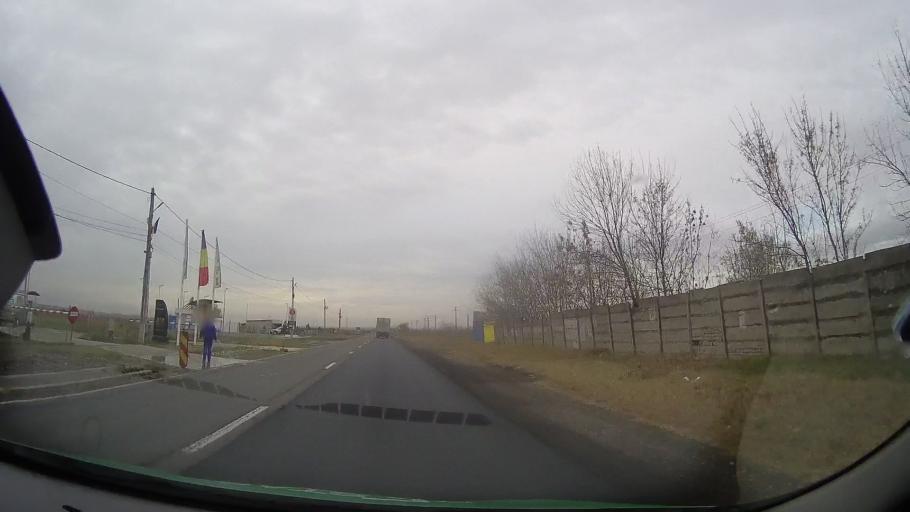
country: RO
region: Prahova
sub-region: Comuna Tomsani
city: Loloiasca
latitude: 44.9663
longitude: 26.2832
